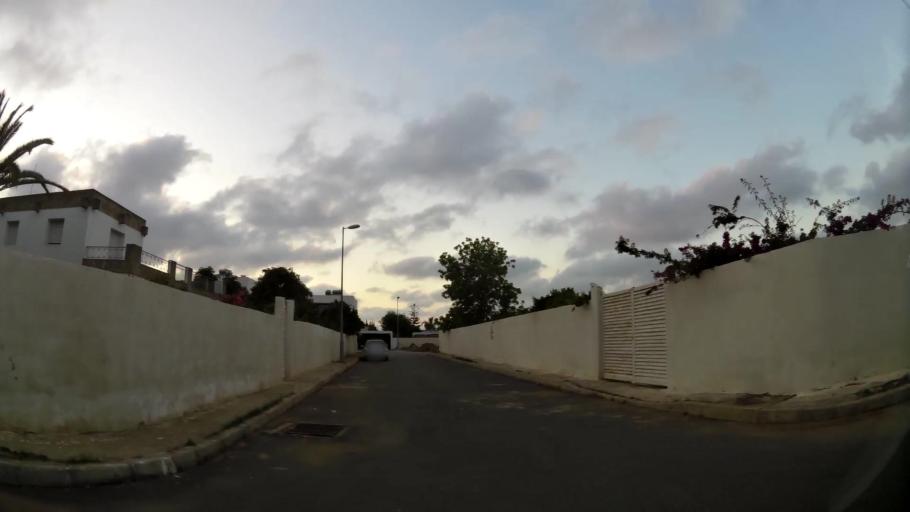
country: MA
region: Rabat-Sale-Zemmour-Zaer
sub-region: Rabat
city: Rabat
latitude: 33.9633
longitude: -6.8335
